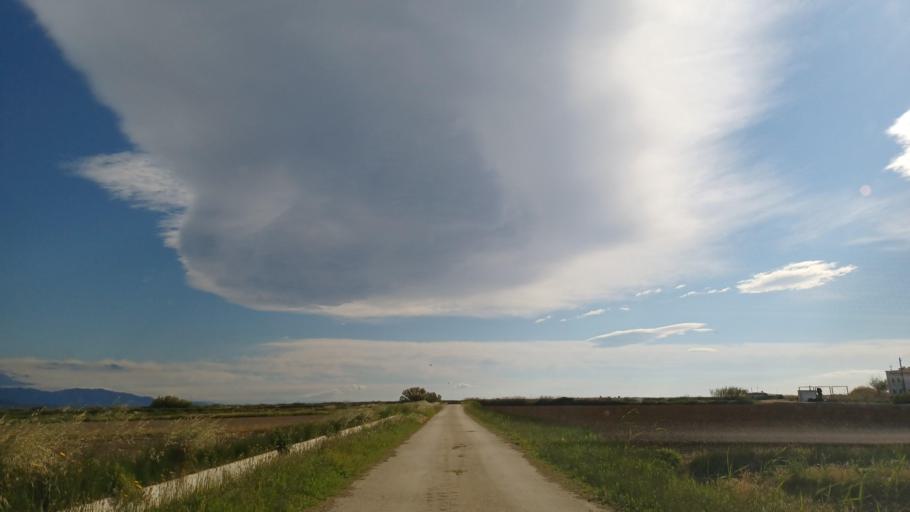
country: ES
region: Catalonia
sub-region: Provincia de Tarragona
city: L'Ampolla
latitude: 40.7780
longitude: 0.7152
